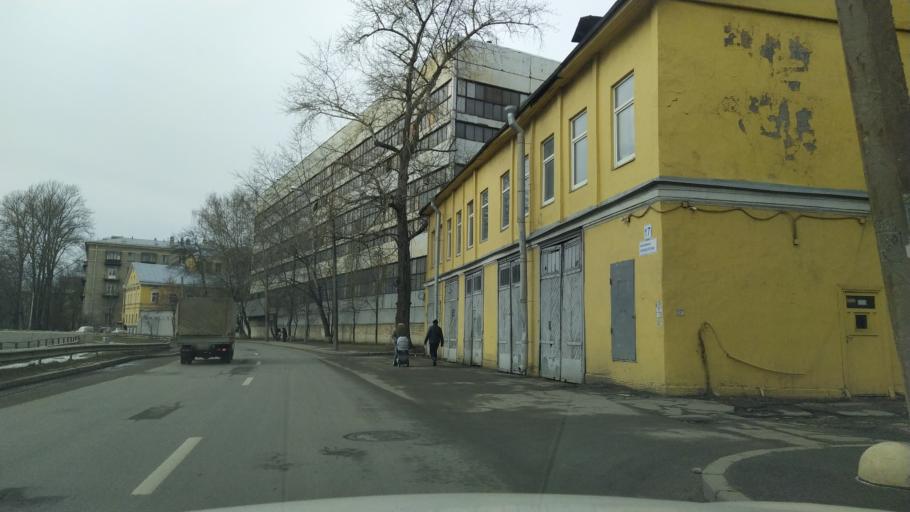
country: RU
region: Leningrad
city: Chernaya Rechka
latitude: 59.9845
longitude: 30.3163
